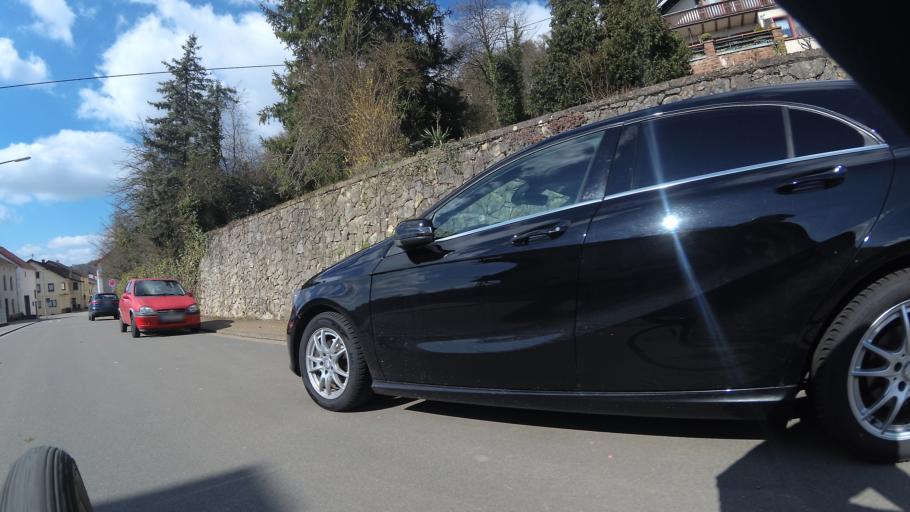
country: DE
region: Saarland
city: Rehlingen-Siersburg
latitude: 49.3579
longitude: 6.6170
